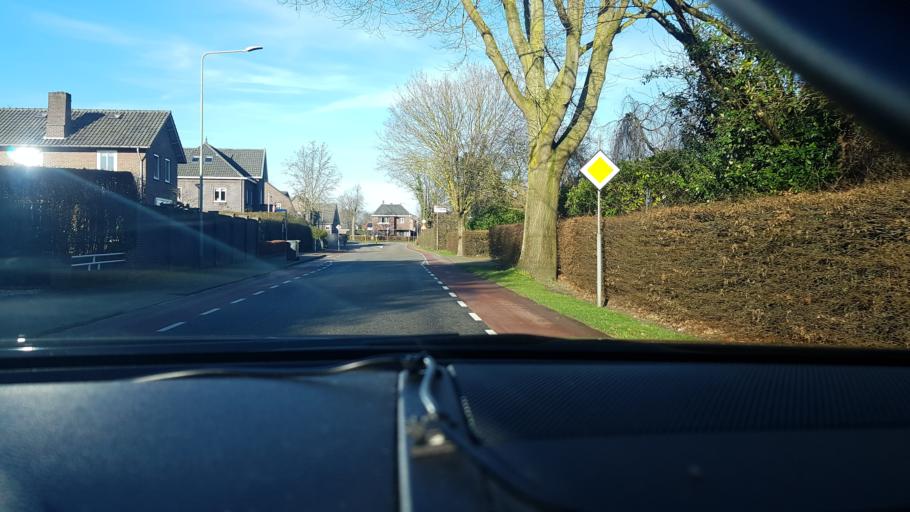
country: NL
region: Limburg
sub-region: Gemeente Peel en Maas
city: Maasbree
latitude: 51.3189
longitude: 6.0033
